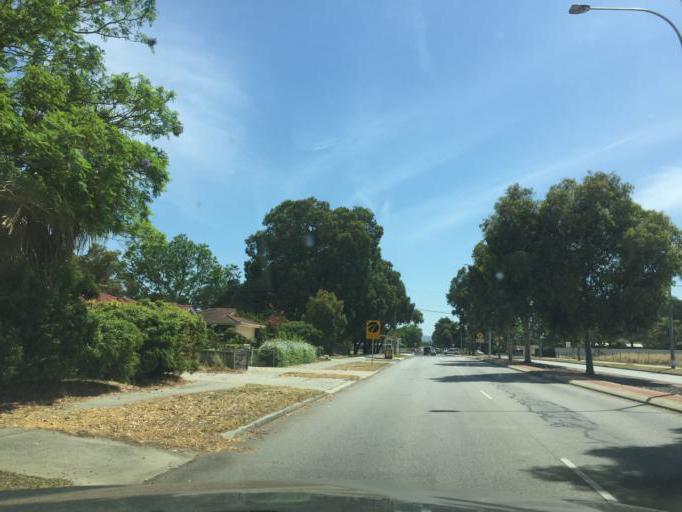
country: AU
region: Western Australia
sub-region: Gosnells
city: Thornlie
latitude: -32.0763
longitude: 115.9597
